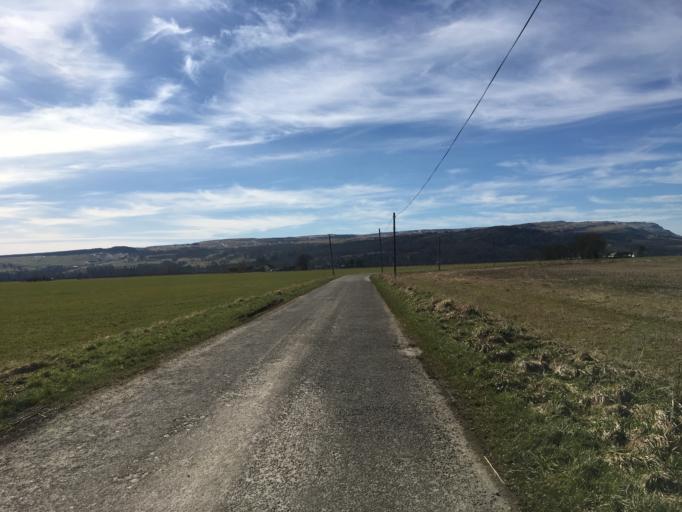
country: GB
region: Scotland
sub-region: Stirling
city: Bridge of Allan
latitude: 56.1323
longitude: -3.9860
